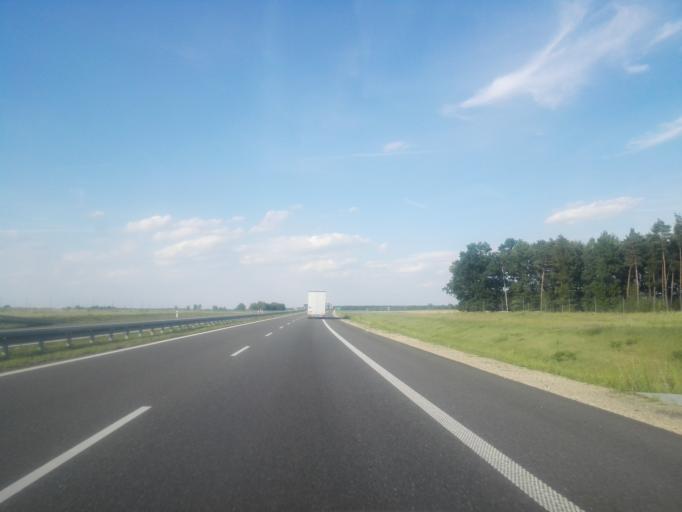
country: PL
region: Lower Silesian Voivodeship
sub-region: Powiat olesnicki
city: Twardogora
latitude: 51.2747
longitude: 17.5589
